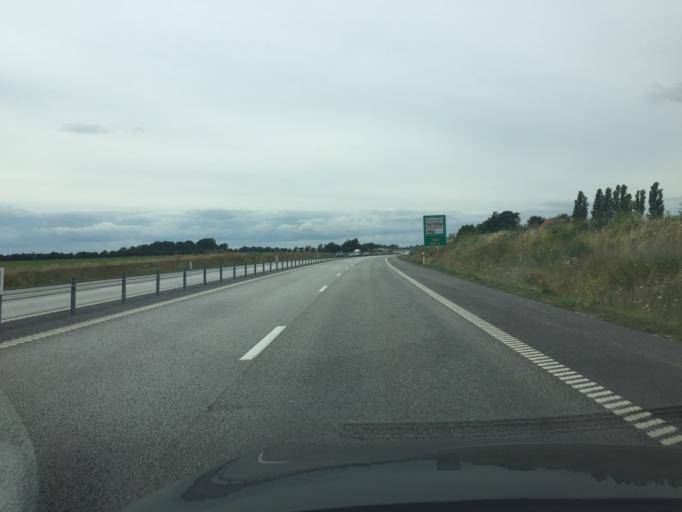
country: SE
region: Skane
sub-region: Trelleborgs Kommun
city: Skare
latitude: 55.4262
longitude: 13.0526
